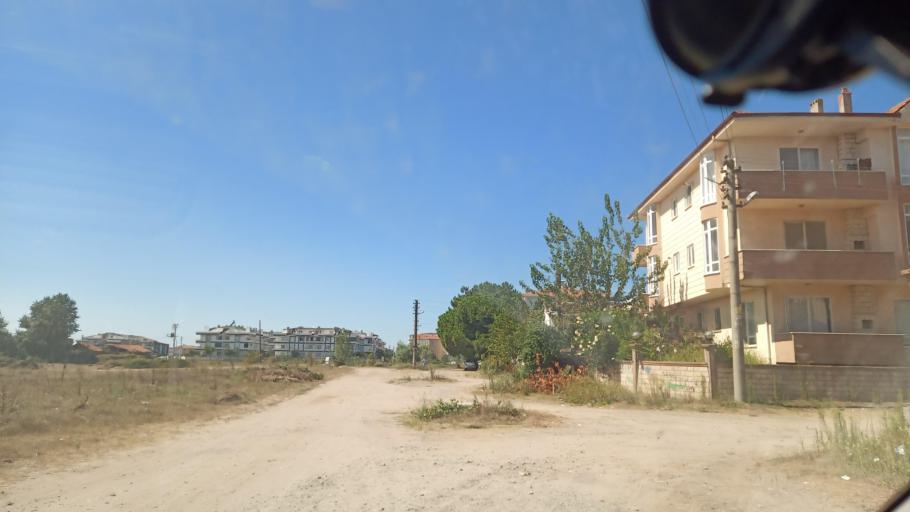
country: TR
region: Sakarya
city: Karasu
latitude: 41.1132
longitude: 30.6785
